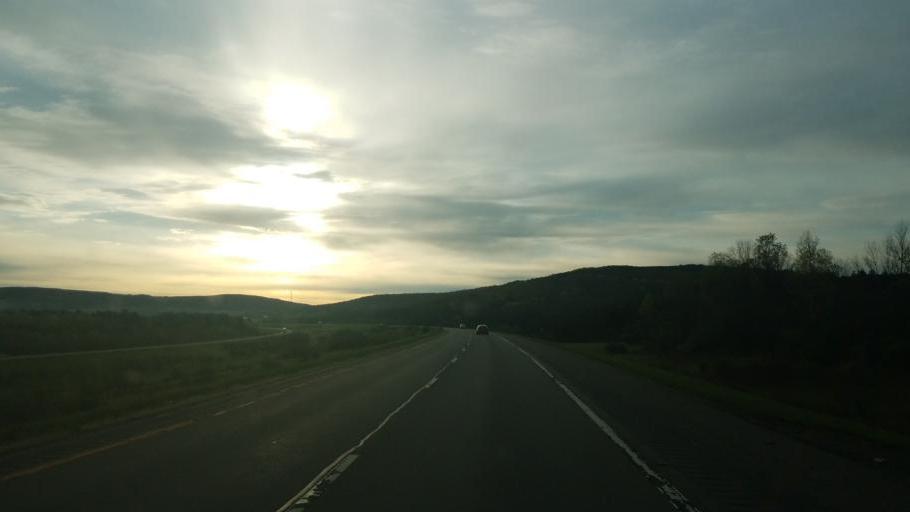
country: US
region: New York
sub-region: Allegany County
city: Belmont
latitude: 42.2926
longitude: -77.9829
